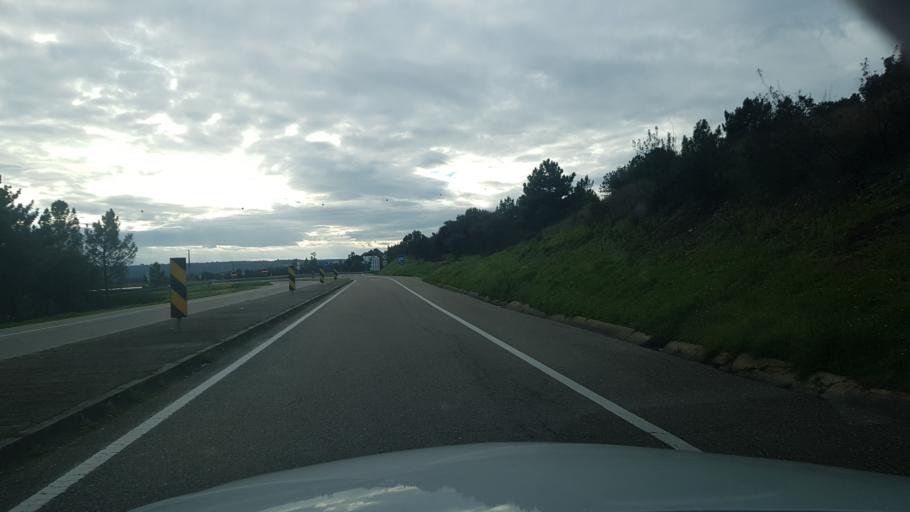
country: PT
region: Santarem
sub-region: Abrantes
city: Tramagal
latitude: 39.4878
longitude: -8.2737
